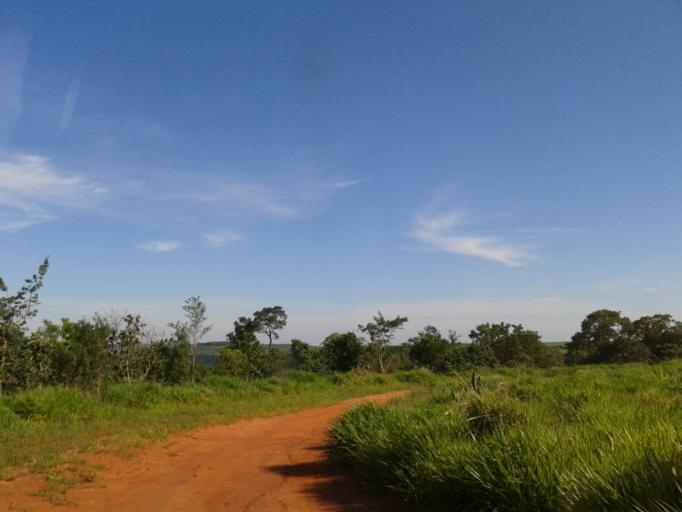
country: BR
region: Minas Gerais
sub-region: Santa Vitoria
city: Santa Vitoria
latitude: -19.1137
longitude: -49.9915
